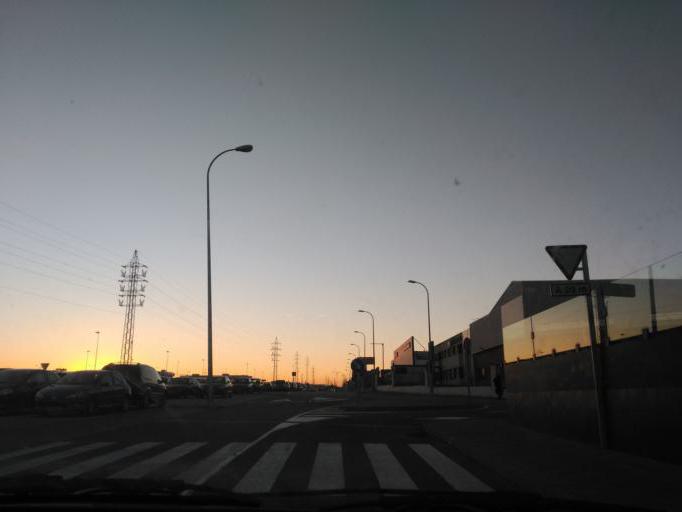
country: ES
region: Castille and Leon
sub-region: Provincia de Salamanca
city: Carbajosa de la Sagrada
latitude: 40.9434
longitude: -5.6521
